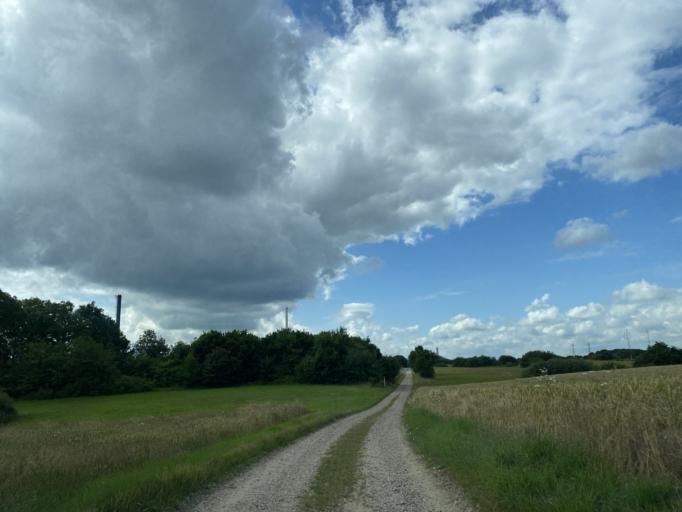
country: DK
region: Central Jutland
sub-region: Silkeborg Kommune
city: Silkeborg
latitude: 56.2092
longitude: 9.5701
